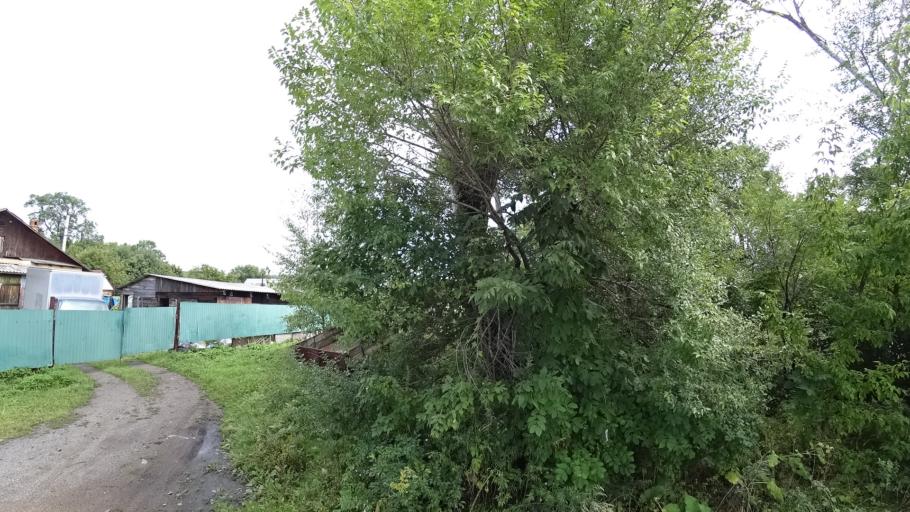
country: RU
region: Primorskiy
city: Lyalichi
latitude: 44.1358
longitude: 132.3728
